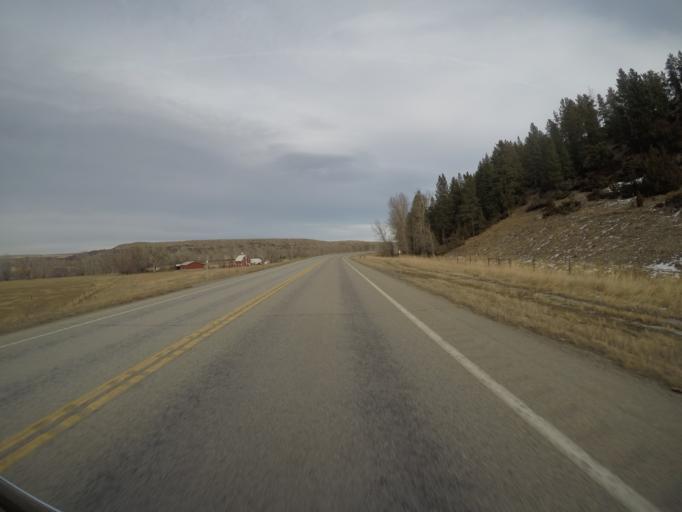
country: US
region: Montana
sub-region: Stillwater County
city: Absarokee
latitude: 45.5420
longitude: -109.4030
